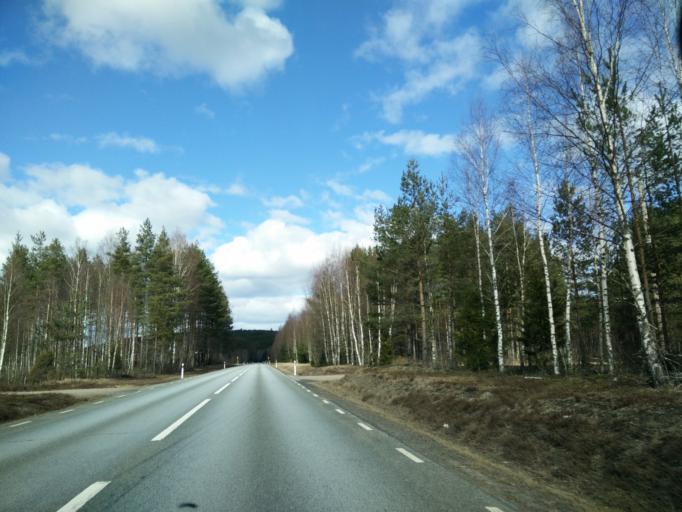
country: SE
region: Vaermland
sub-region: Munkfors Kommun
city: Munkfors
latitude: 59.9388
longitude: 13.5796
